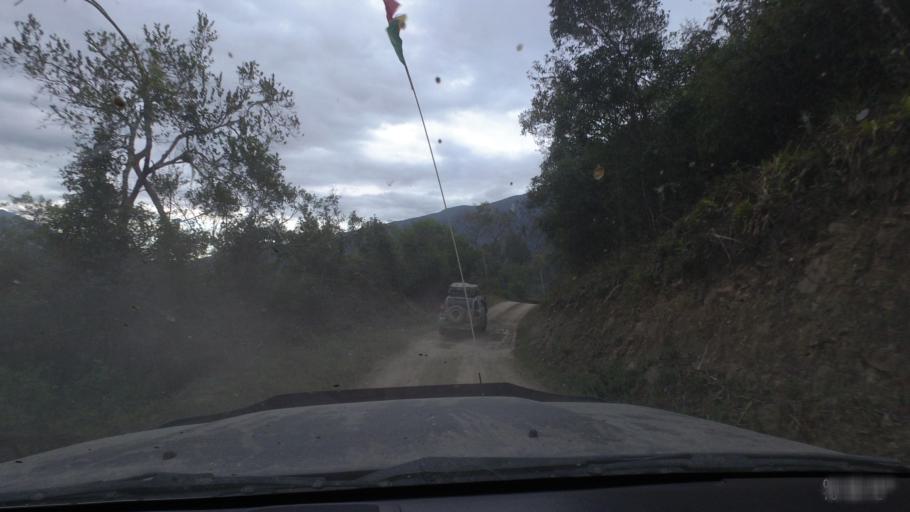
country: BO
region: La Paz
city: Quime
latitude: -16.5201
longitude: -66.7706
